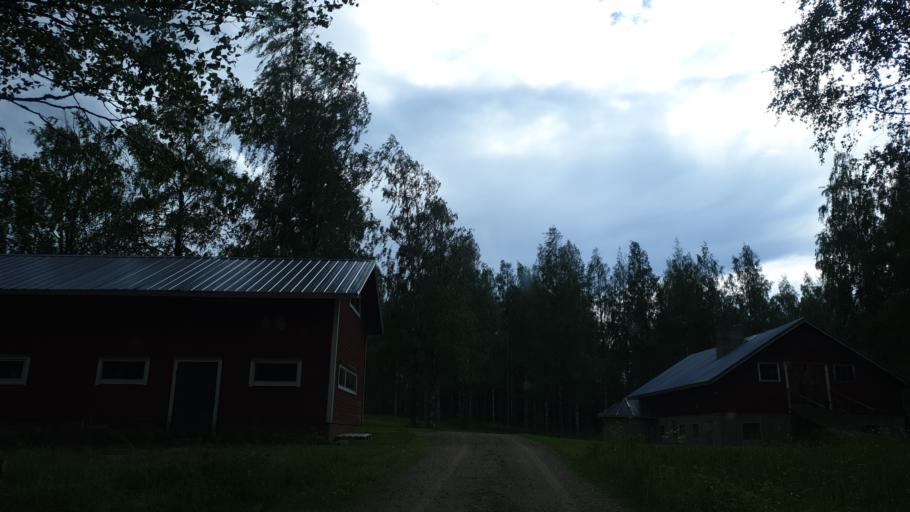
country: FI
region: Northern Savo
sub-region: Koillis-Savo
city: Kaavi
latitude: 62.9758
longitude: 28.7546
